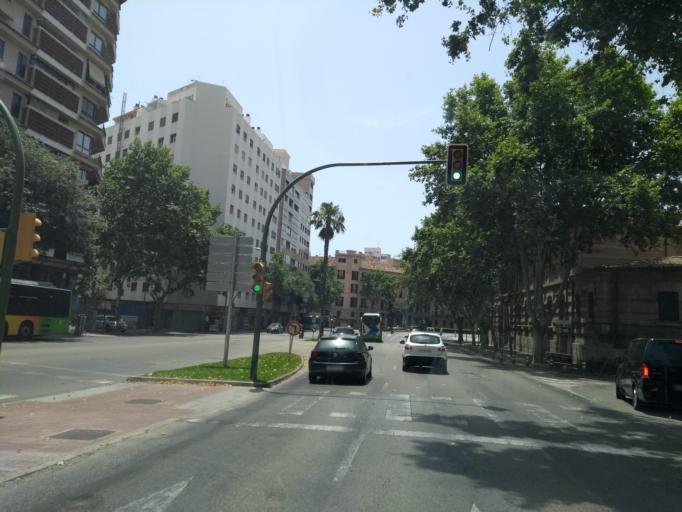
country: ES
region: Balearic Islands
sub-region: Illes Balears
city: Palma
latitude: 39.5775
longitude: 2.6477
